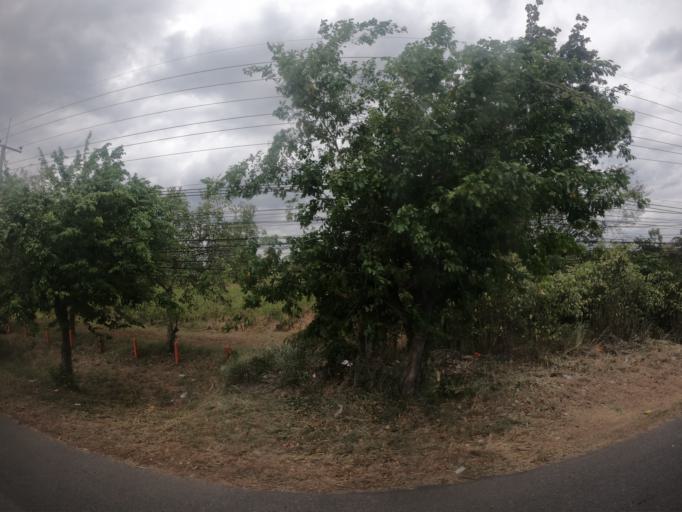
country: TH
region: Nakhon Ratchasima
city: Nakhon Ratchasima
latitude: 14.8724
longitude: 102.1797
